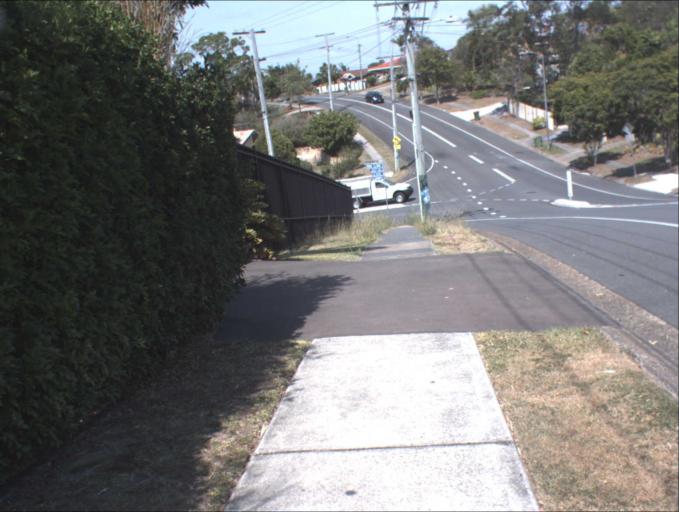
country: AU
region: Queensland
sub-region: Logan
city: Slacks Creek
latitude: -27.6578
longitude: 153.1877
